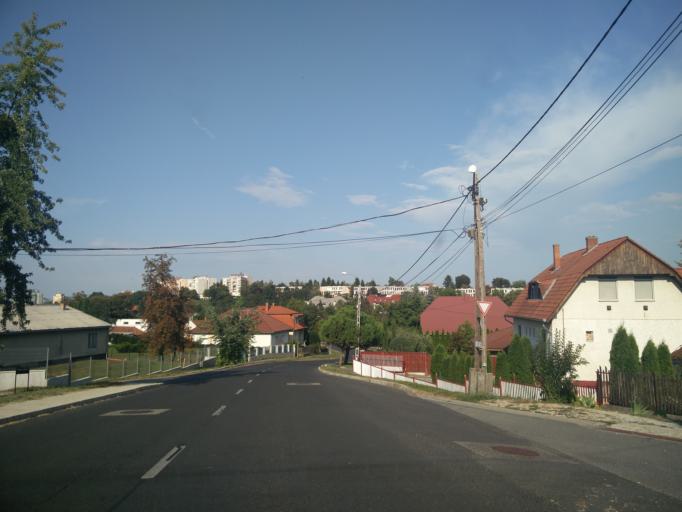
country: HU
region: Zala
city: Zalaegerszeg
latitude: 46.8296
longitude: 16.8246
